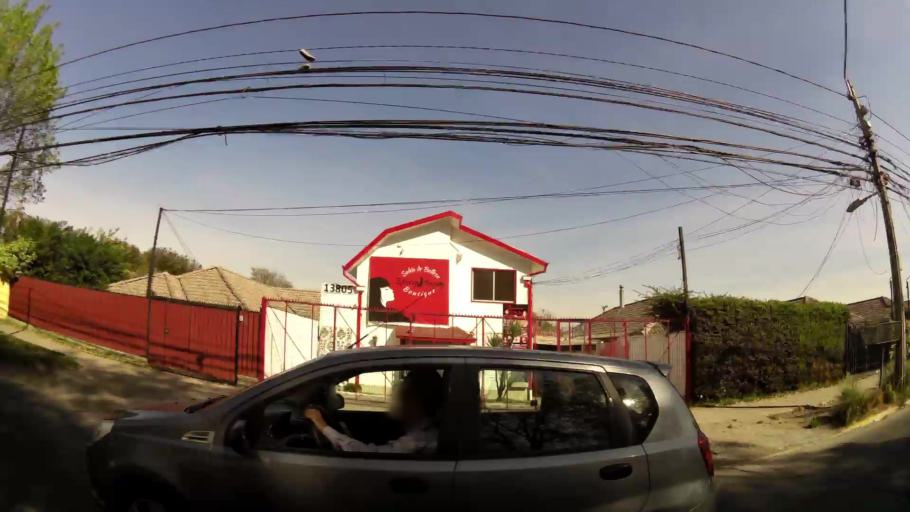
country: CL
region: Santiago Metropolitan
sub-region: Provincia de Santiago
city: Villa Presidente Frei, Nunoa, Santiago, Chile
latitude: -33.5014
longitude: -70.5610
